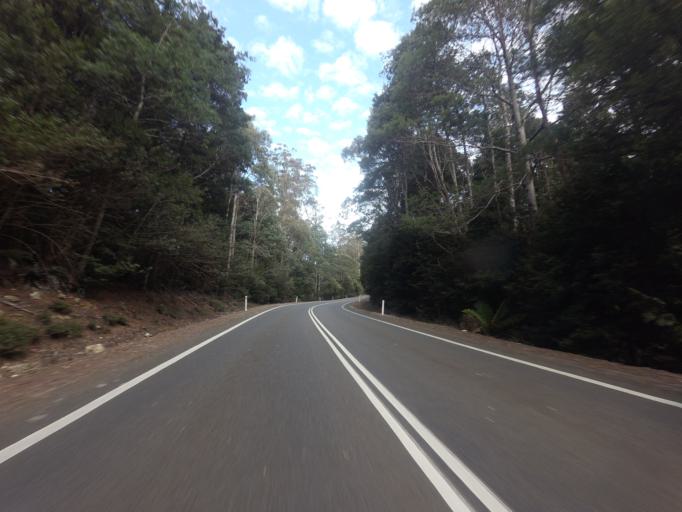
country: AU
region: Tasmania
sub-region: Meander Valley
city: Deloraine
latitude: -41.6562
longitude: 146.7221
